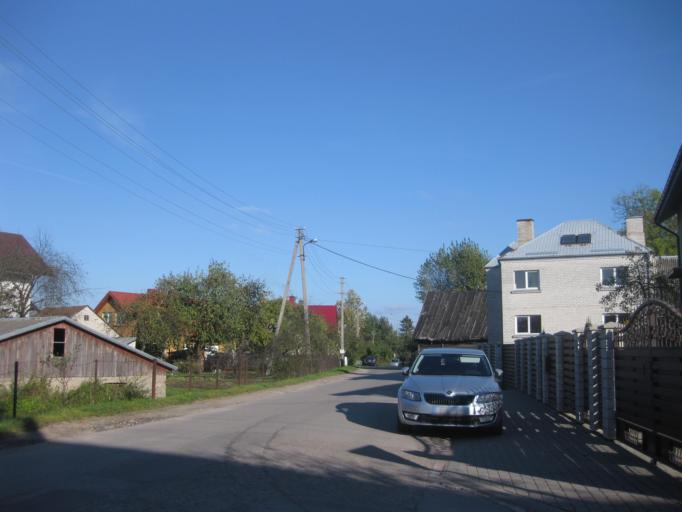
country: LT
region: Kauno apskritis
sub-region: Kauno rajonas
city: Garliava
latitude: 54.8376
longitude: 23.8749
